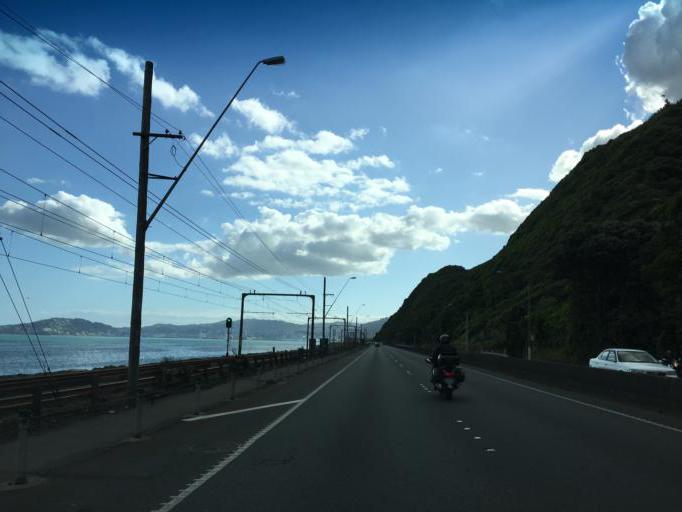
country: NZ
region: Wellington
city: Petone
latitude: -41.2368
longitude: 174.8316
